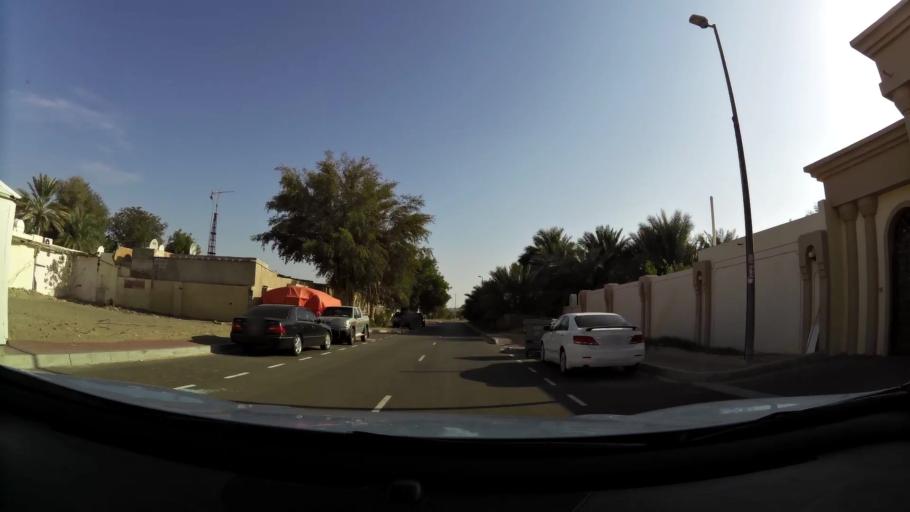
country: AE
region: Abu Dhabi
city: Al Ain
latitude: 24.0418
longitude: 55.8396
